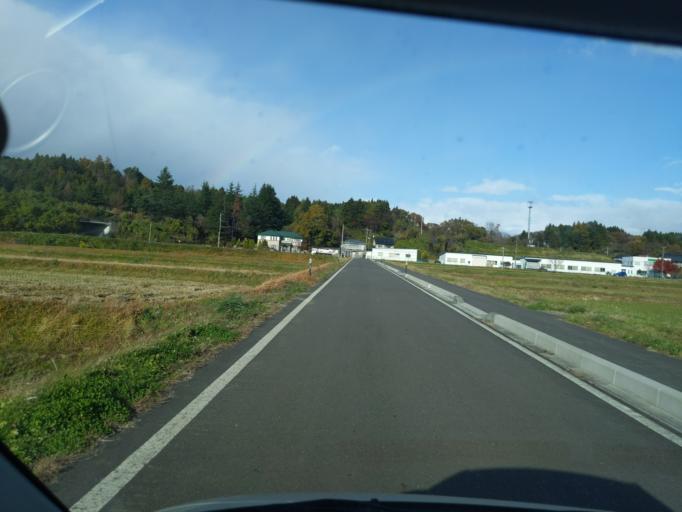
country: JP
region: Iwate
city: Ichinoseki
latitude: 39.0154
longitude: 141.0998
